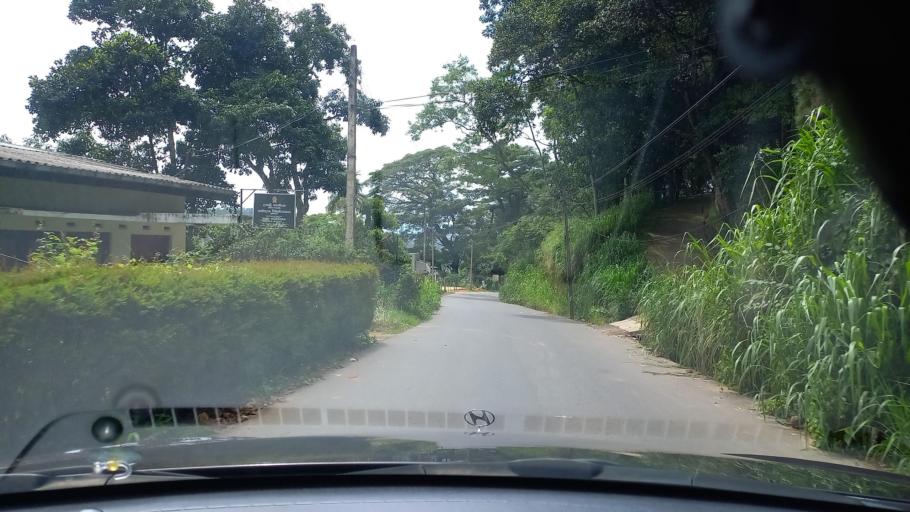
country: LK
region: Central
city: Kandy
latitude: 7.2334
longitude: 80.6038
